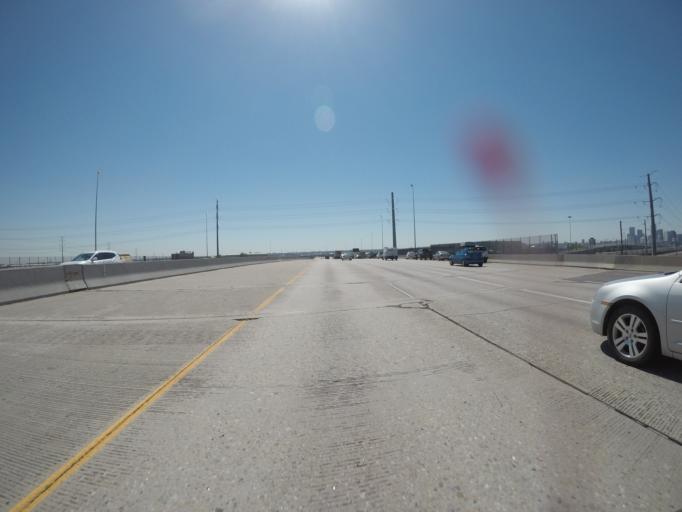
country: US
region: Colorado
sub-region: Adams County
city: Berkley
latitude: 39.7824
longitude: -104.9983
